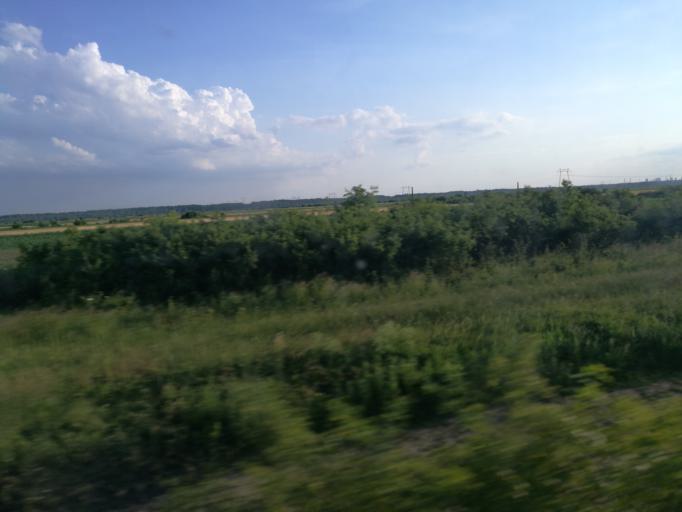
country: RO
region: Arges
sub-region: Comuna Calinesti
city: Calinesti
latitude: 44.8168
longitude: 25.0425
